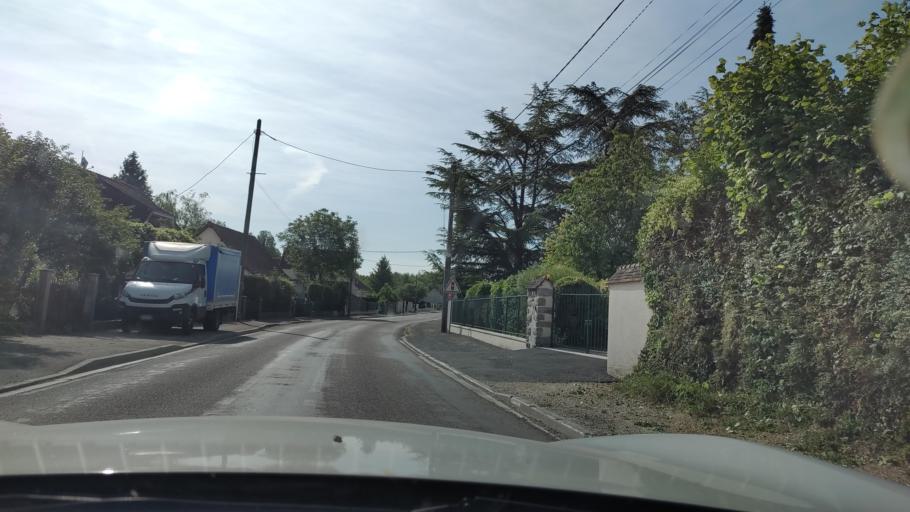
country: FR
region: Champagne-Ardenne
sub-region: Departement de l'Aube
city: Nogent-sur-Seine
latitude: 48.4730
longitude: 3.5584
